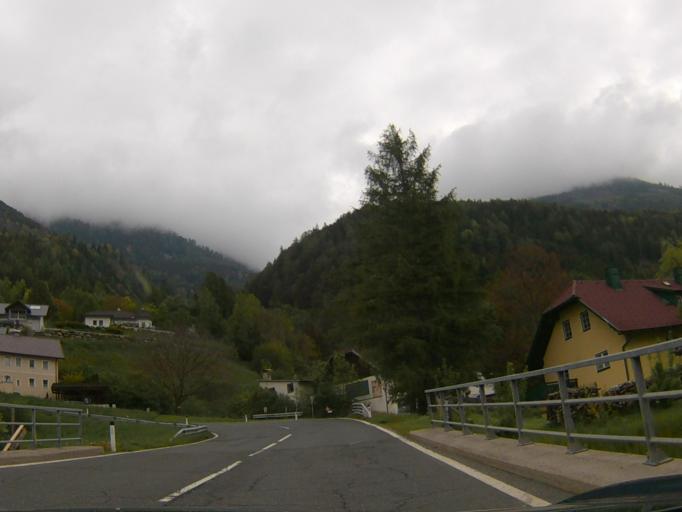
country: AT
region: Carinthia
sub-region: Politischer Bezirk Spittal an der Drau
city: Obervellach
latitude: 46.9351
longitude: 13.1988
